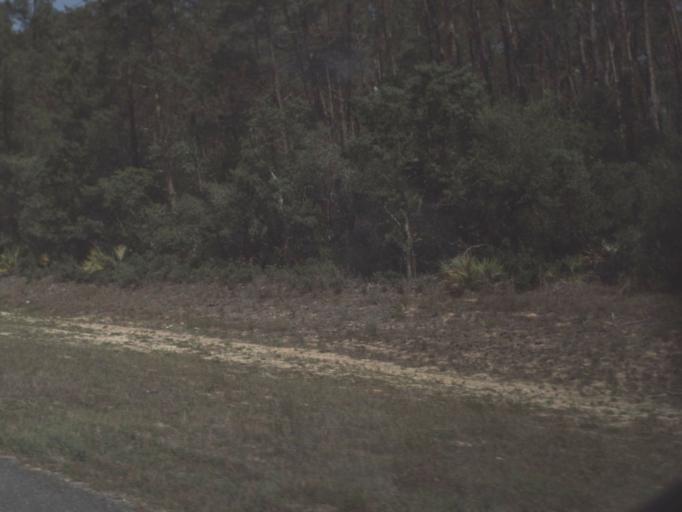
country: US
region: Florida
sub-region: Marion County
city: Silver Springs Shores
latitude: 29.1766
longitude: -81.8170
